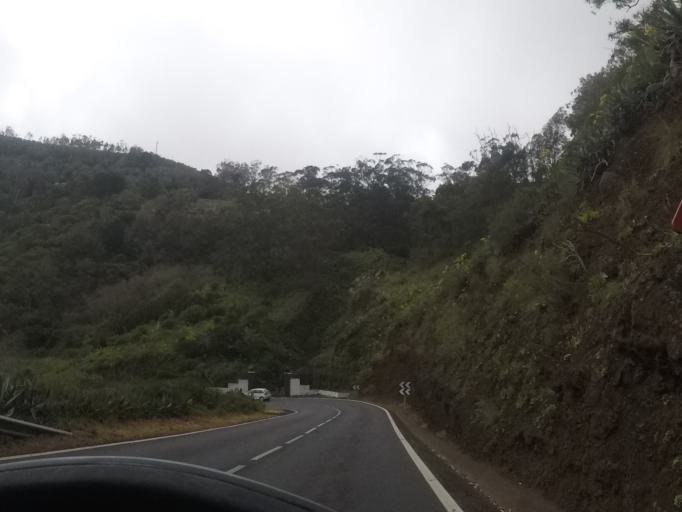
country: ES
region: Canary Islands
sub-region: Provincia de Santa Cruz de Tenerife
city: Tacoronte
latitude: 28.5037
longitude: -16.3789
